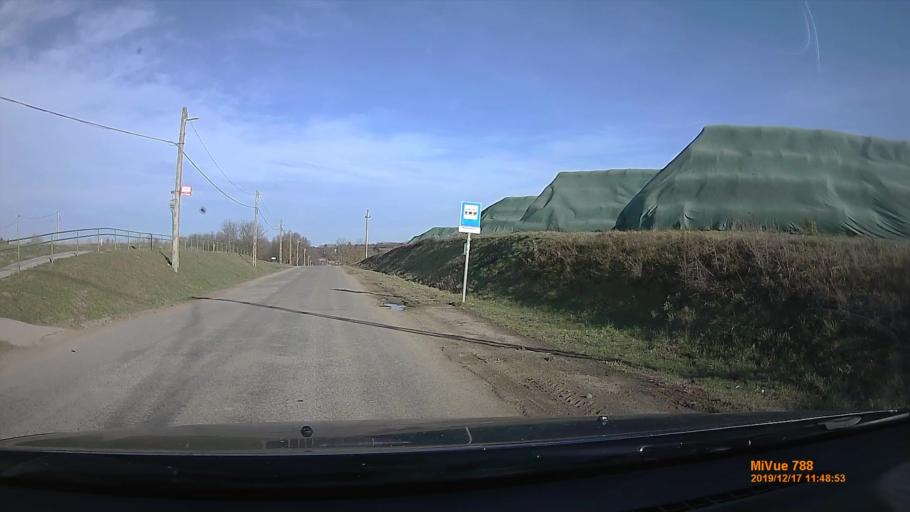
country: HU
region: Somogy
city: Kaposvar
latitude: 46.4530
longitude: 17.7656
